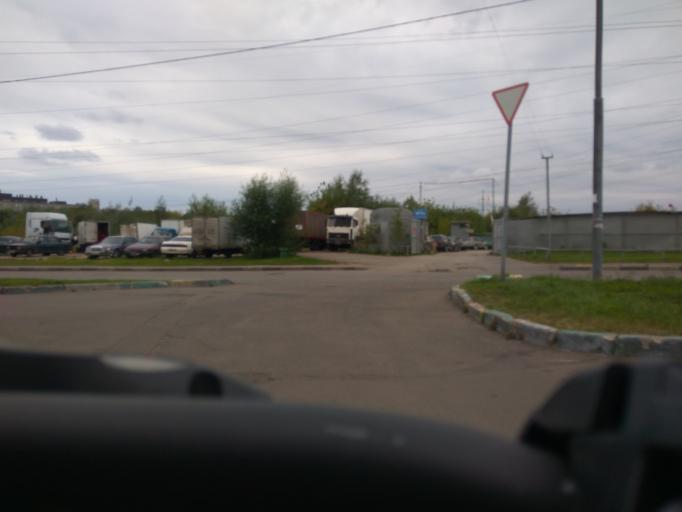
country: RU
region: Moscow
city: Tsaritsyno
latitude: 55.6441
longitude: 37.6497
